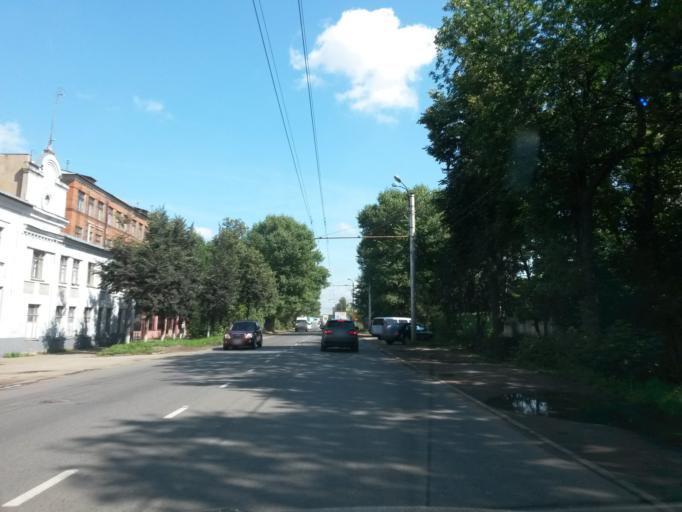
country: RU
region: Ivanovo
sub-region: Gorod Ivanovo
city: Ivanovo
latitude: 57.0056
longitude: 40.9482
